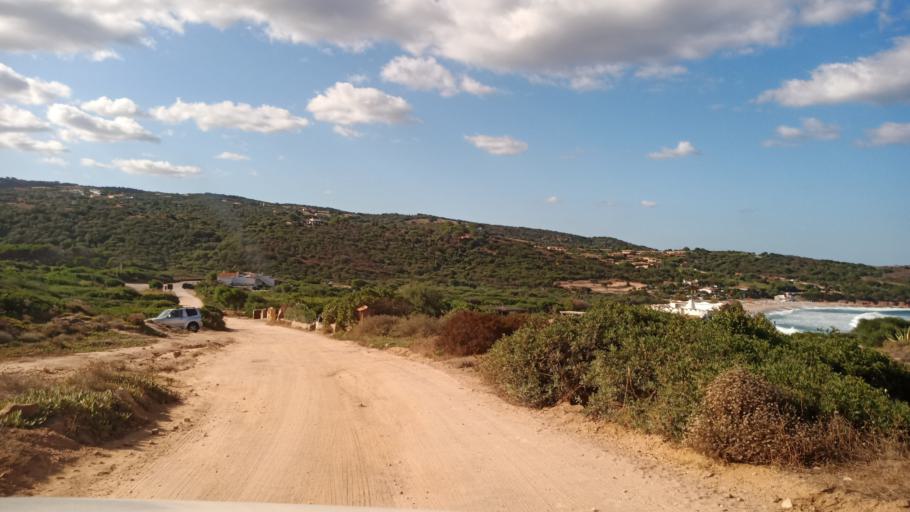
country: IT
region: Sardinia
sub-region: Provincia di Olbia-Tempio
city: Trinita d'Agultu
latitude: 41.0181
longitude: 8.8904
